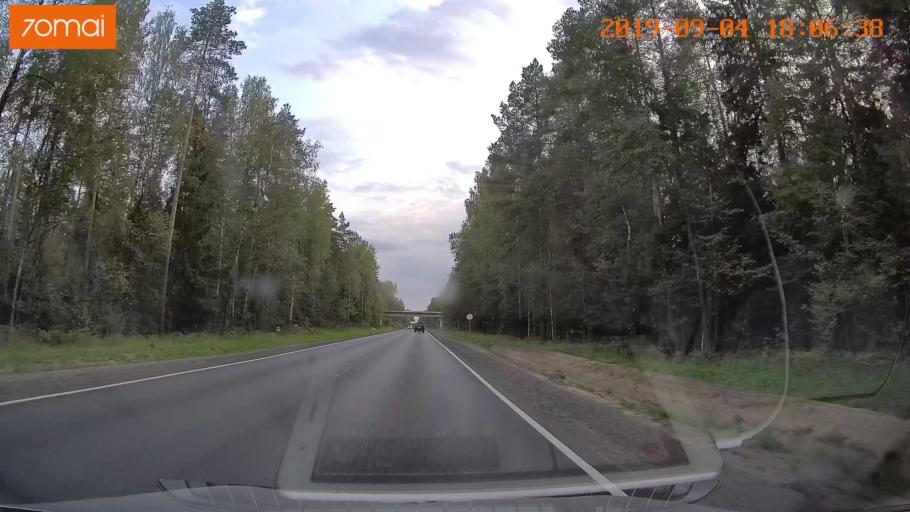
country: RU
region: Moskovskaya
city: Khorlovo
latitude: 55.4290
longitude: 38.8122
